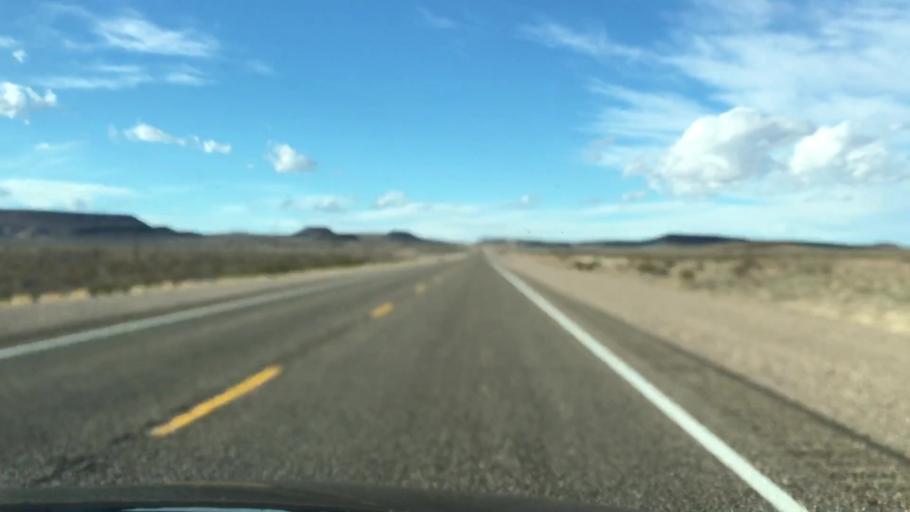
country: US
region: Nevada
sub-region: Esmeralda County
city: Goldfield
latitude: 37.3585
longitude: -117.1139
